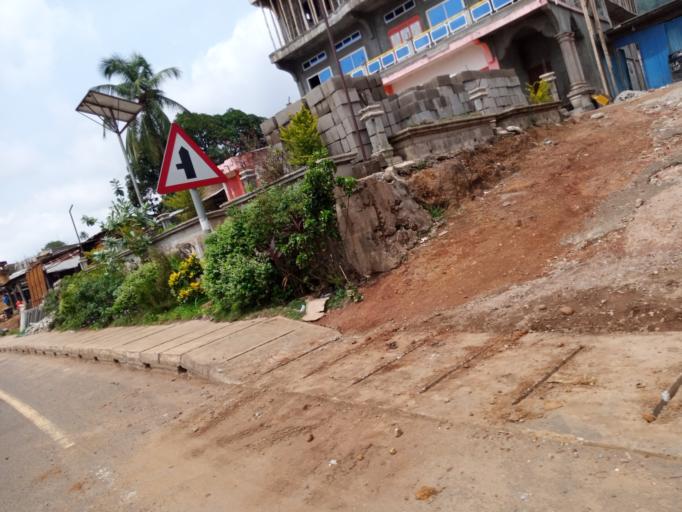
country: SL
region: Western Area
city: Waterloo
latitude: 8.3583
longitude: -13.0826
